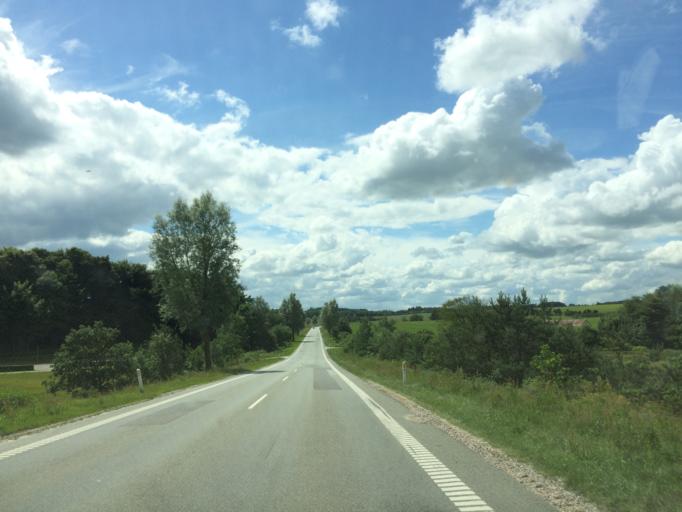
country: DK
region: North Denmark
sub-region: Mariagerfjord Kommune
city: Hobro
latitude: 56.6207
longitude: 9.7229
